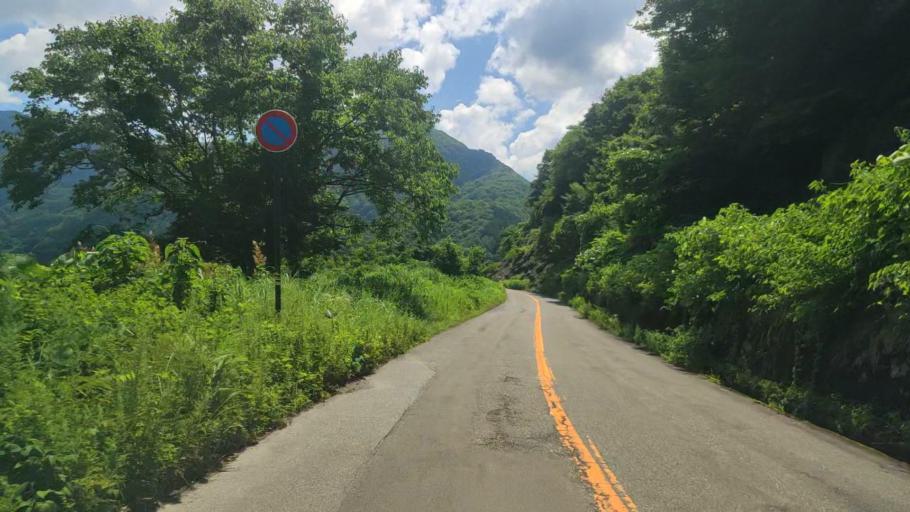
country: JP
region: Fukui
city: Ono
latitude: 35.9144
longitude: 136.5290
